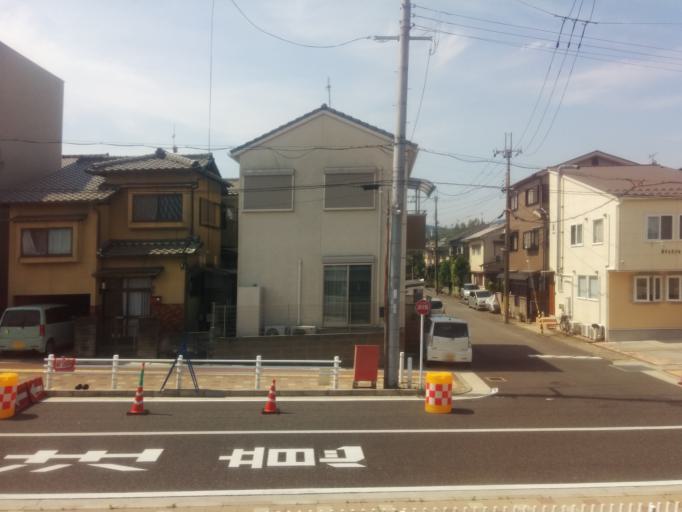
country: JP
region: Kyoto
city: Kameoka
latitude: 35.0109
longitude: 135.5920
